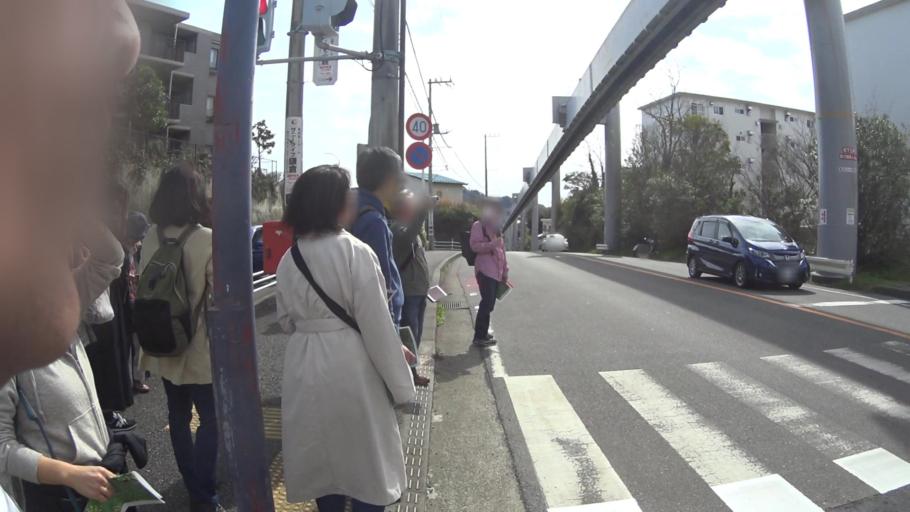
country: JP
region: Kanagawa
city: Kamakura
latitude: 35.3358
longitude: 139.5223
